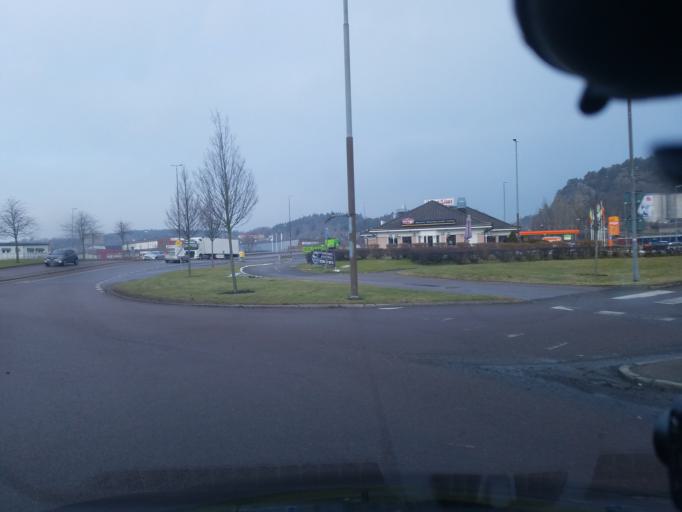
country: SE
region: Vaestra Goetaland
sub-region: Uddevalla Kommun
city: Uddevalla
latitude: 58.3530
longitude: 11.9160
